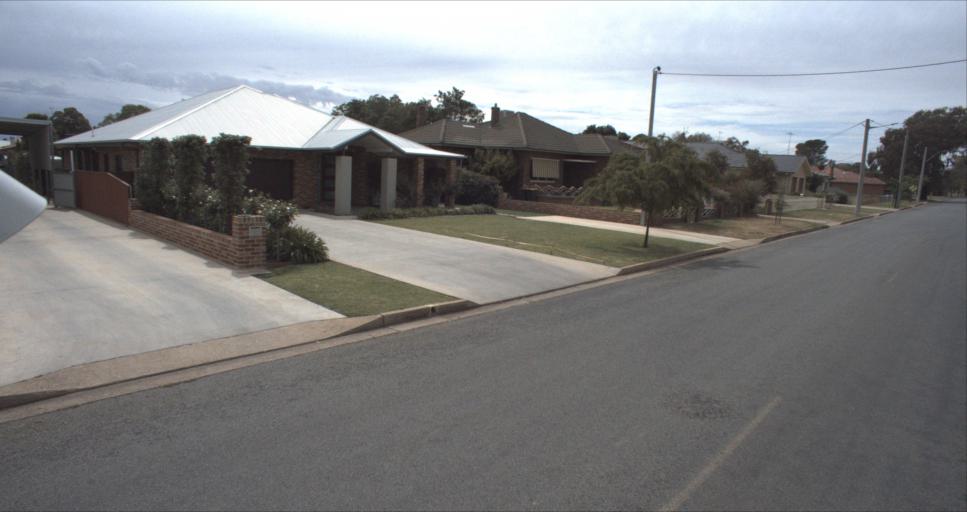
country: AU
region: New South Wales
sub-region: Leeton
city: Leeton
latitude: -34.5478
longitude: 146.4021
